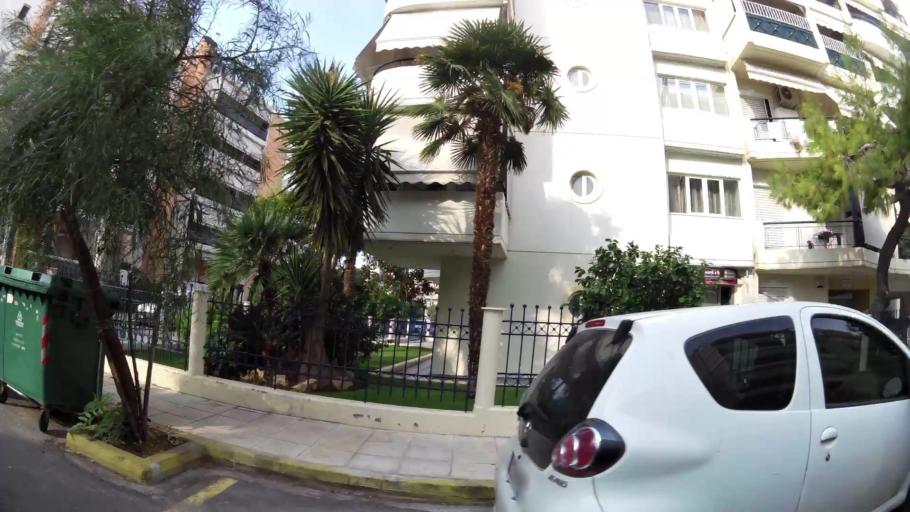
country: GR
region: Attica
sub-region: Nomarchia Athinas
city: Kallithea
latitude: 37.9549
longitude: 23.6890
